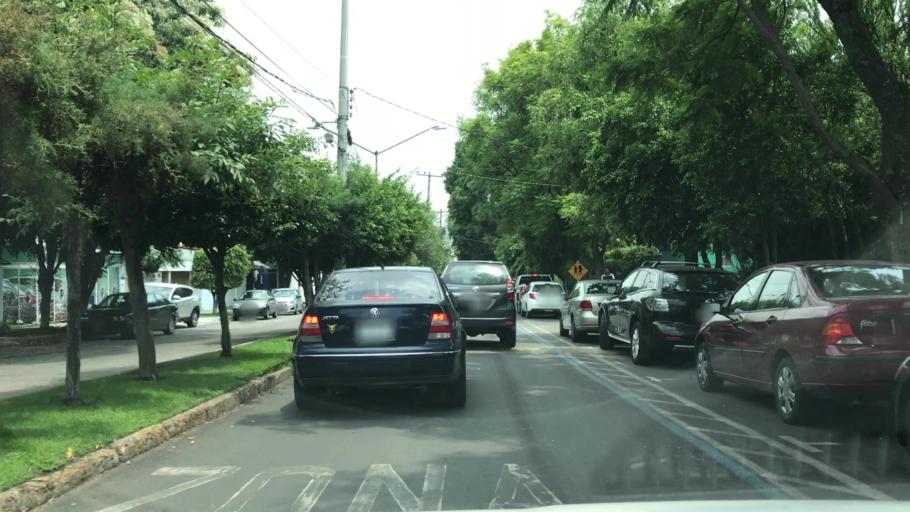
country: MX
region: Jalisco
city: Guadalajara
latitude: 20.6602
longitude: -103.4065
